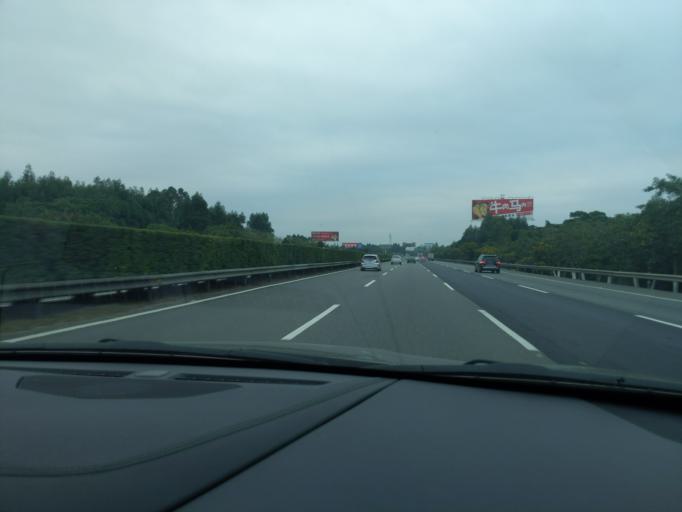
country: CN
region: Fujian
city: Neikeng
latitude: 24.7659
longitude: 118.4506
